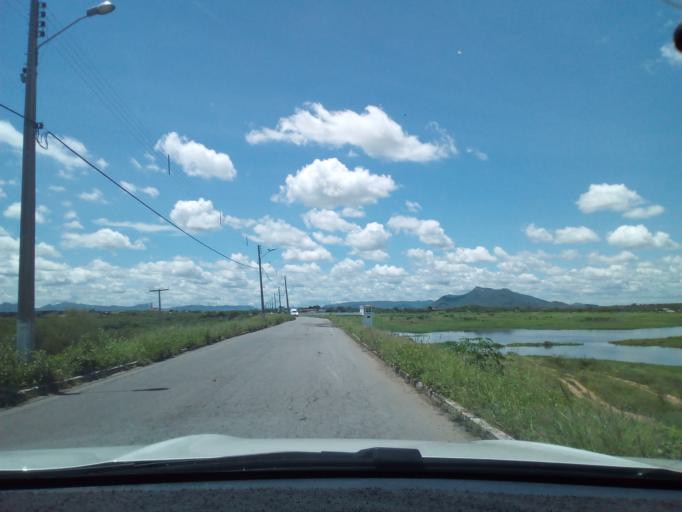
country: BR
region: Rio Grande do Norte
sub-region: Caico
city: Caico
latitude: -6.4937
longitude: -37.0682
